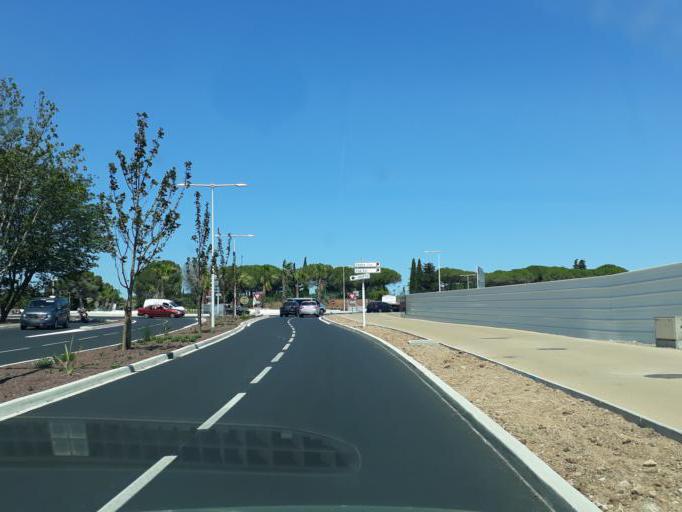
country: FR
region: Languedoc-Roussillon
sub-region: Departement de l'Herault
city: Le Cap d'Agde
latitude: 43.2880
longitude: 3.5073
